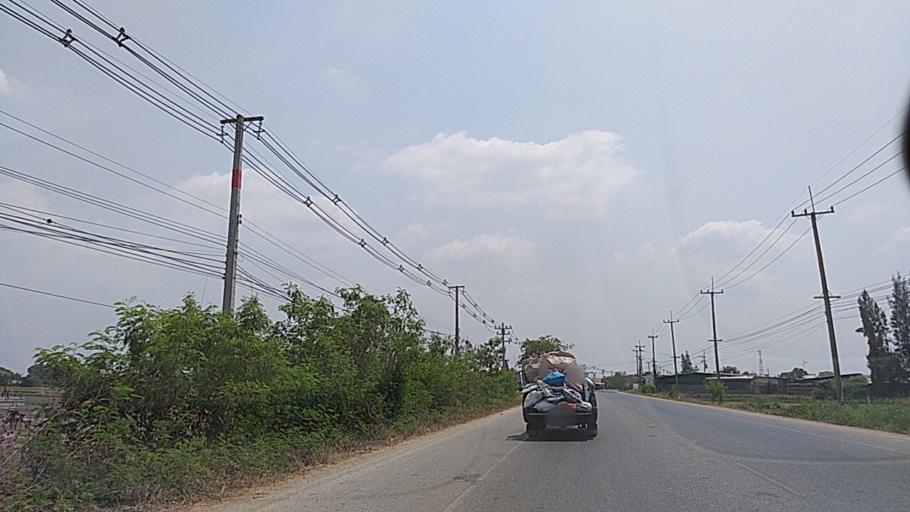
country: TH
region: Chachoengsao
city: Chachoengsao
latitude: 13.7623
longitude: 101.0721
